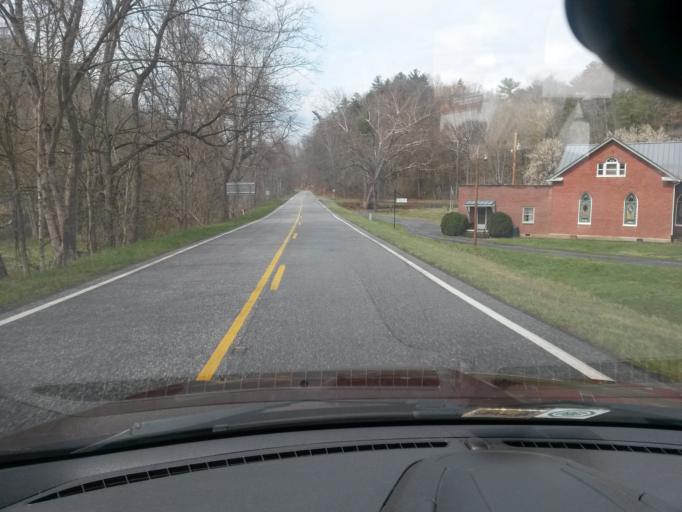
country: US
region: Virginia
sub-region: Bath County
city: Warm Springs
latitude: 38.0017
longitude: -79.6328
